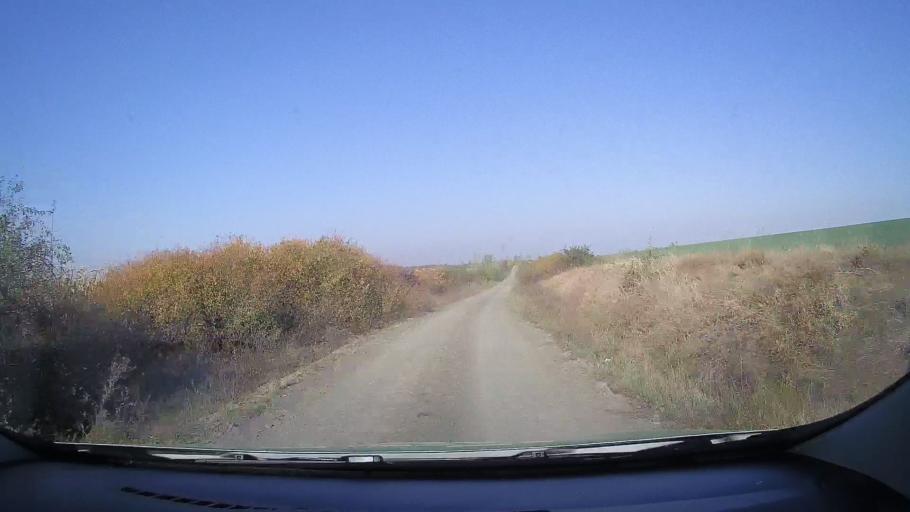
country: RO
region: Satu Mare
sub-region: Comuna Sauca
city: Sauca
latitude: 47.4819
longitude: 22.4671
